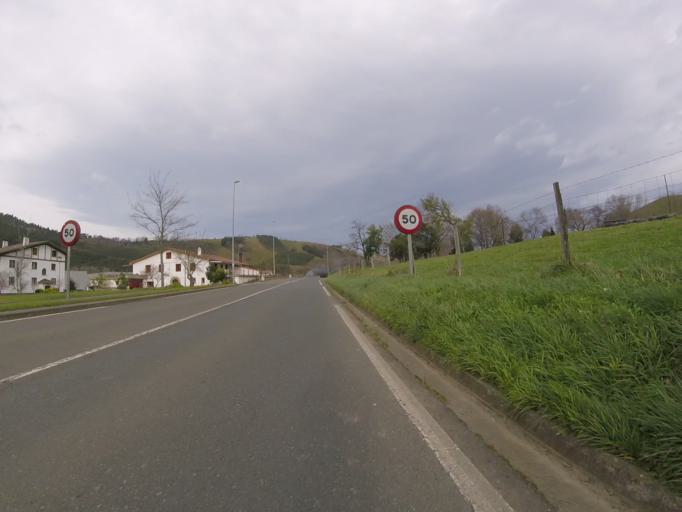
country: ES
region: Basque Country
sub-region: Provincia de Guipuzcoa
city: Aizarnazabal
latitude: 43.2612
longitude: -2.2379
